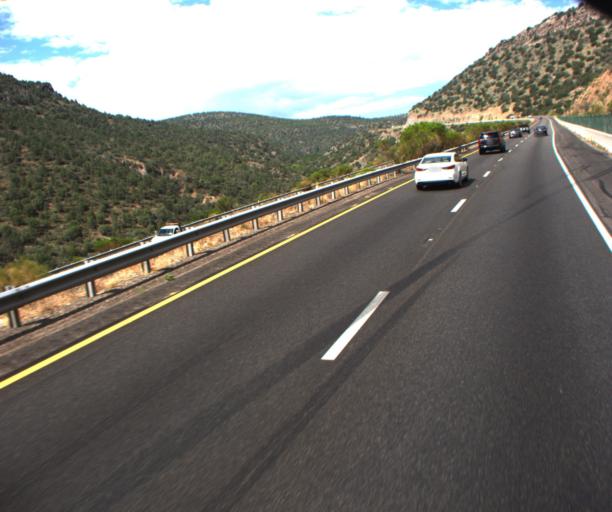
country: US
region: Arizona
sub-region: Yavapai County
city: Camp Verde
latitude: 34.5356
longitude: -111.9317
